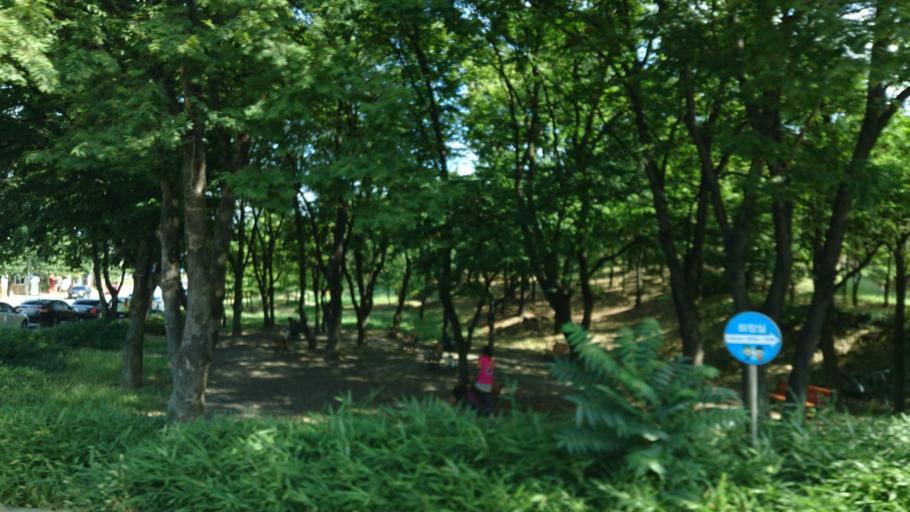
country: KR
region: Daegu
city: Daegu
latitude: 35.8766
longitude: 128.6560
